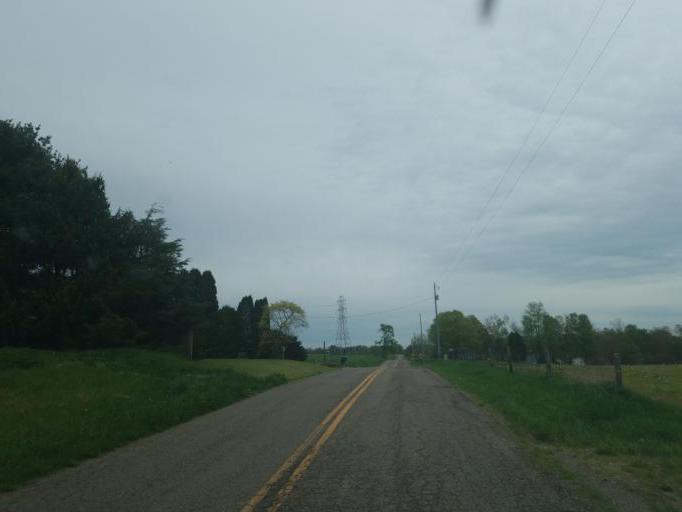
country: US
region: Ohio
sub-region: Sandusky County
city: Bellville
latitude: 40.5383
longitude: -82.4237
